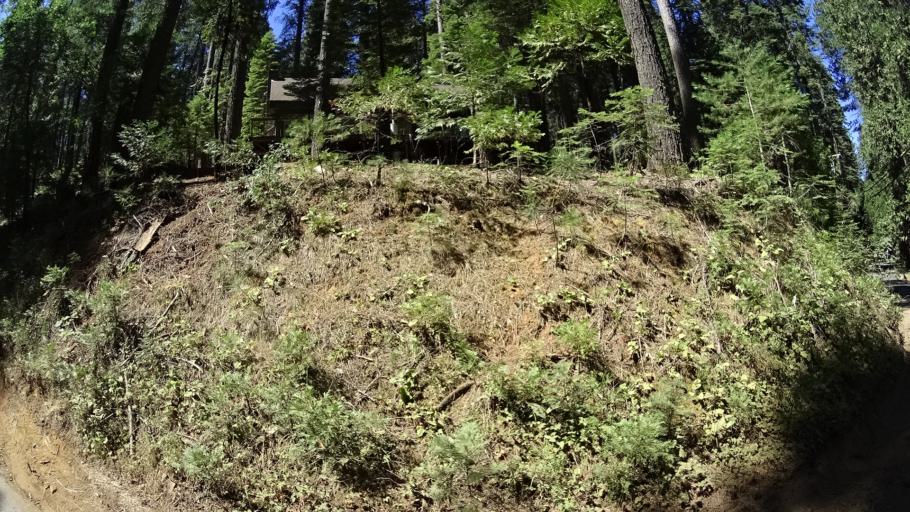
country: US
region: California
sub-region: Calaveras County
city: Arnold
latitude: 38.2338
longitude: -120.3407
